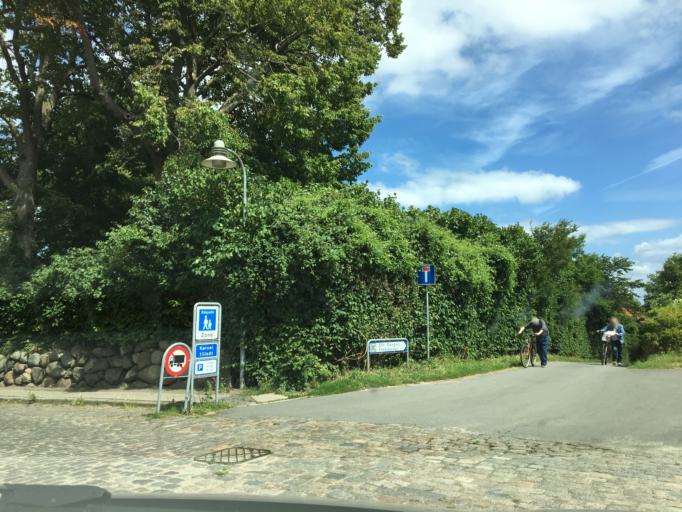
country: DK
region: South Denmark
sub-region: Langeland Kommune
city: Rudkobing
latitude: 54.9353
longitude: 10.7106
